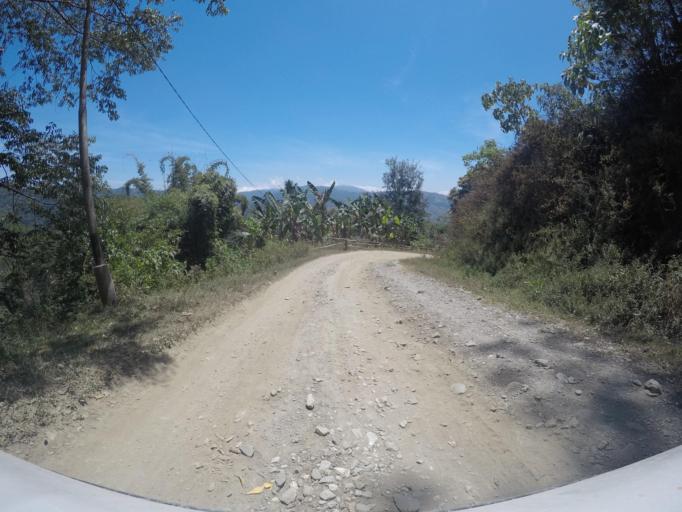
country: TL
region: Ermera
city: Gleno
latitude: -8.7403
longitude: 125.4066
